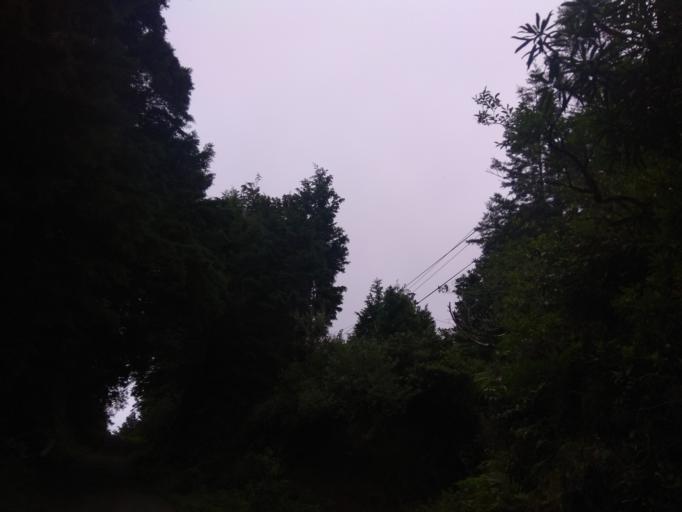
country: CR
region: Heredia
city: San Josecito
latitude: 10.0702
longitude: -84.0832
